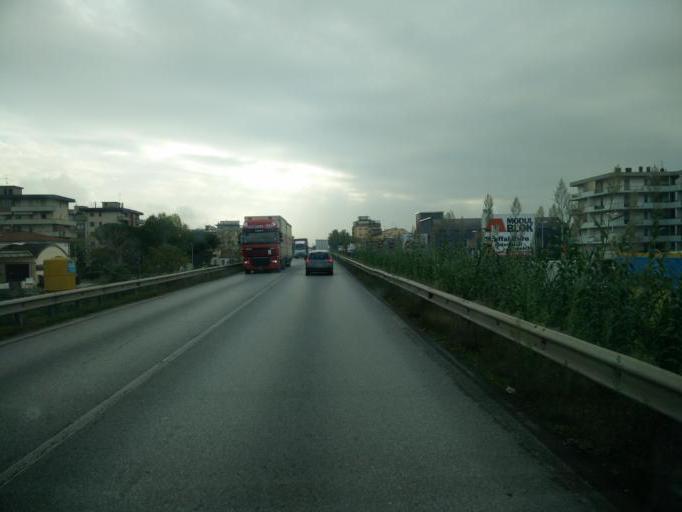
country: IT
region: Tuscany
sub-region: Provincia di Prato
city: Prato
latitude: 43.8718
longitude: 11.0846
